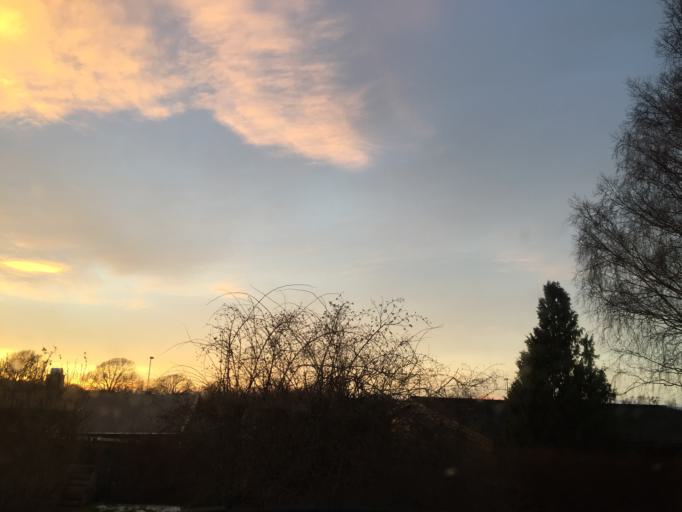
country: NO
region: Ostfold
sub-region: Moss
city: Moss
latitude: 59.4366
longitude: 10.6103
